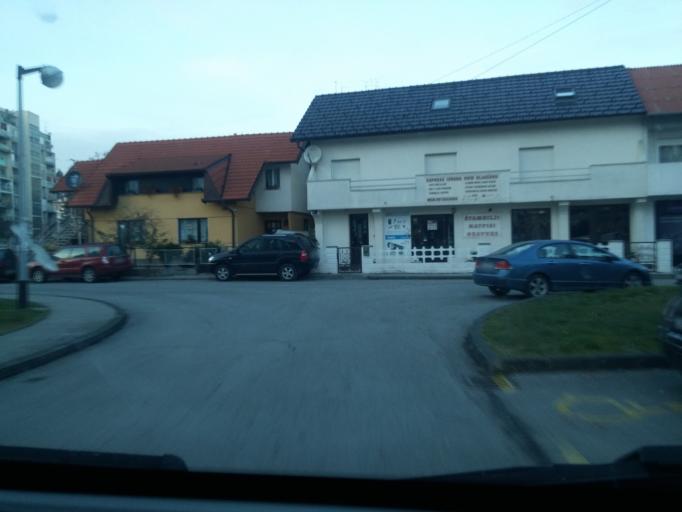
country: HR
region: Grad Zagreb
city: Stenjevec
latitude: 45.8169
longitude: 15.8774
